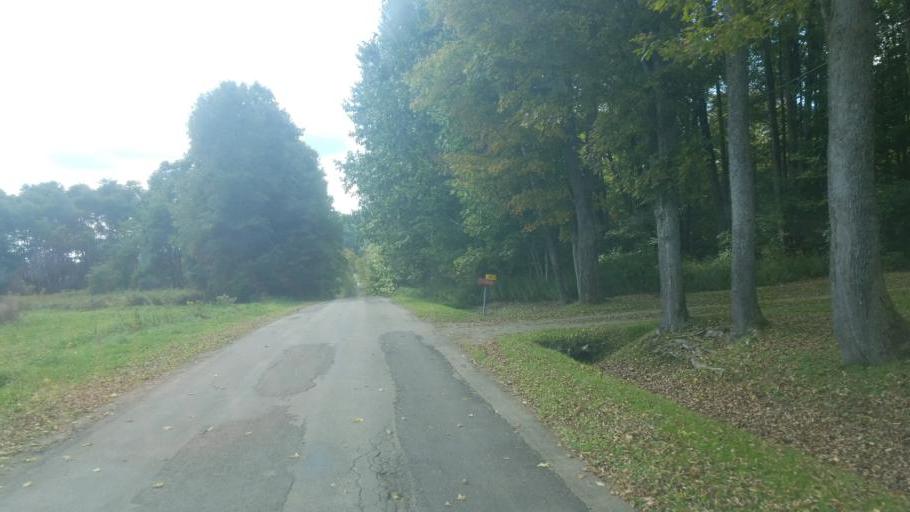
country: US
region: New York
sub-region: Cattaraugus County
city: Franklinville
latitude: 42.2137
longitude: -78.4147
